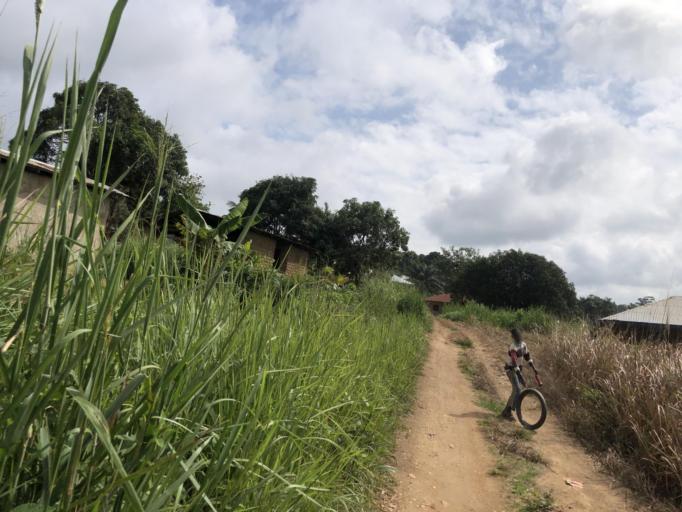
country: SL
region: Eastern Province
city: Kailahun
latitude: 8.2807
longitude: -10.5650
